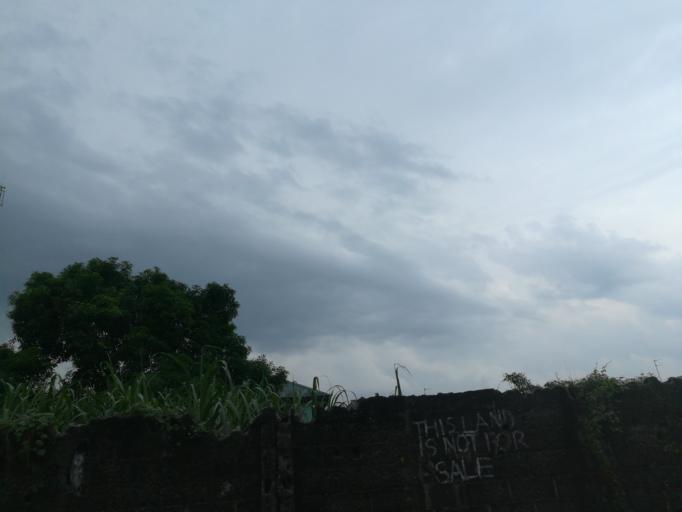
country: NG
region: Rivers
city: Port Harcourt
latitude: 4.8770
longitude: 6.9986
